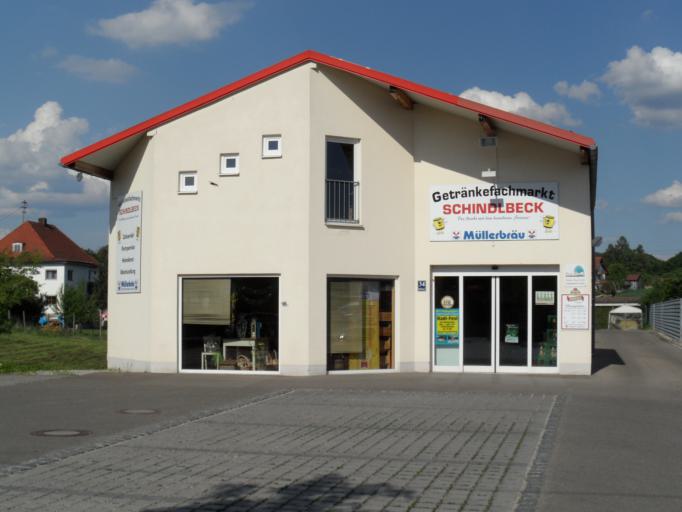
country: DE
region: Bavaria
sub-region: Upper Bavaria
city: Pfaffenhofen an der Ilm
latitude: 48.5400
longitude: 11.5157
